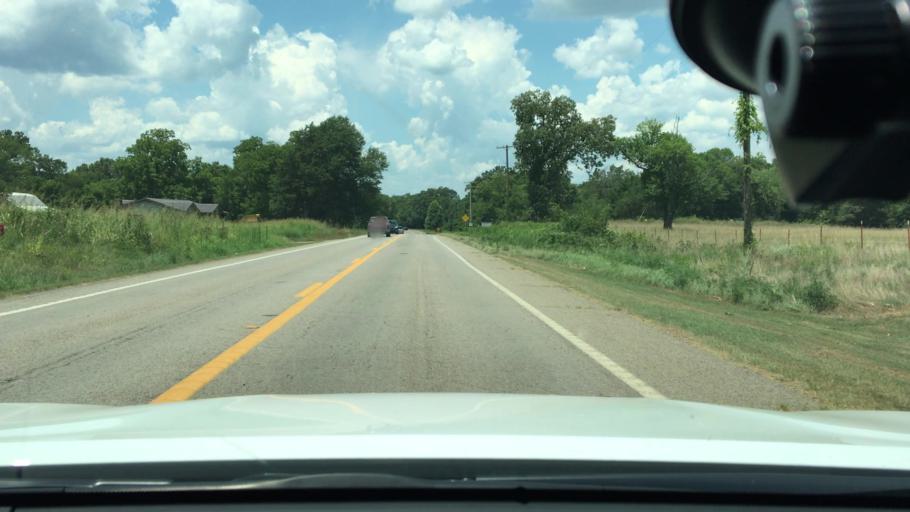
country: US
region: Arkansas
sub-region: Logan County
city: Booneville
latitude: 35.1508
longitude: -93.8261
